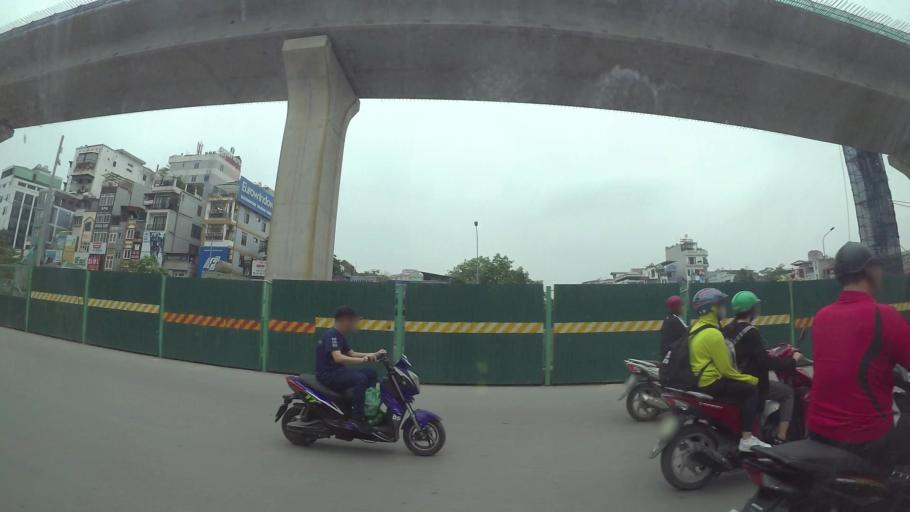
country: VN
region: Ha Noi
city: Hai BaTrung
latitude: 20.9987
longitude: 105.8384
